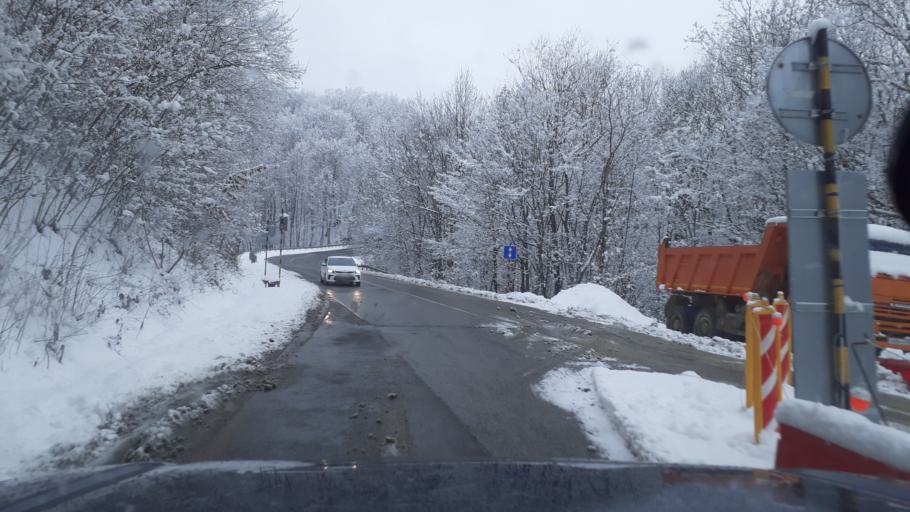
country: RU
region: Adygeya
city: Kamennomostskiy
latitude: 44.1923
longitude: 40.1705
